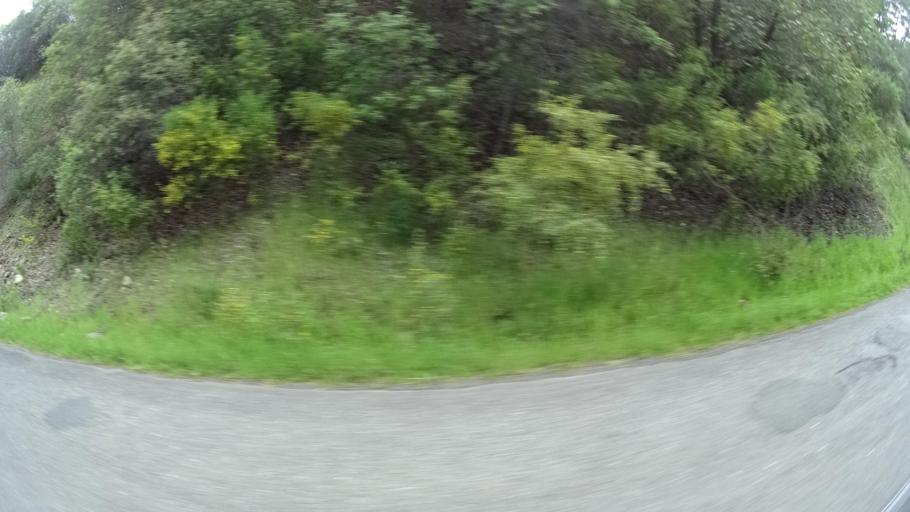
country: US
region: California
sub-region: Humboldt County
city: Redway
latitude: 40.1932
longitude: -123.5907
